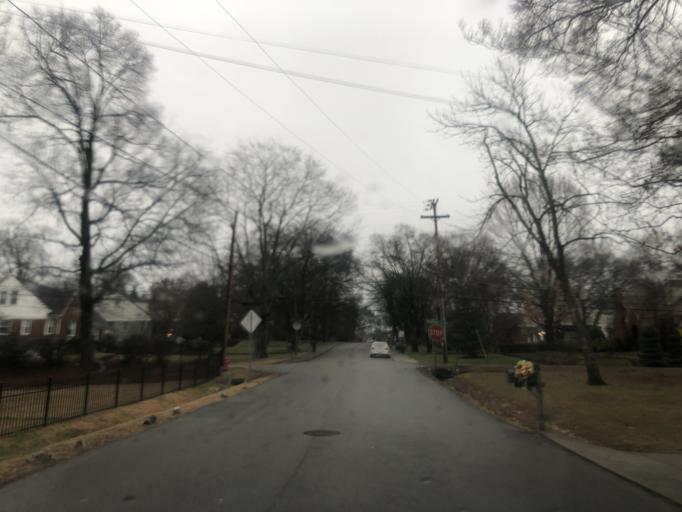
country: US
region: Tennessee
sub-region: Davidson County
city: Oak Hill
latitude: 36.1230
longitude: -86.8030
